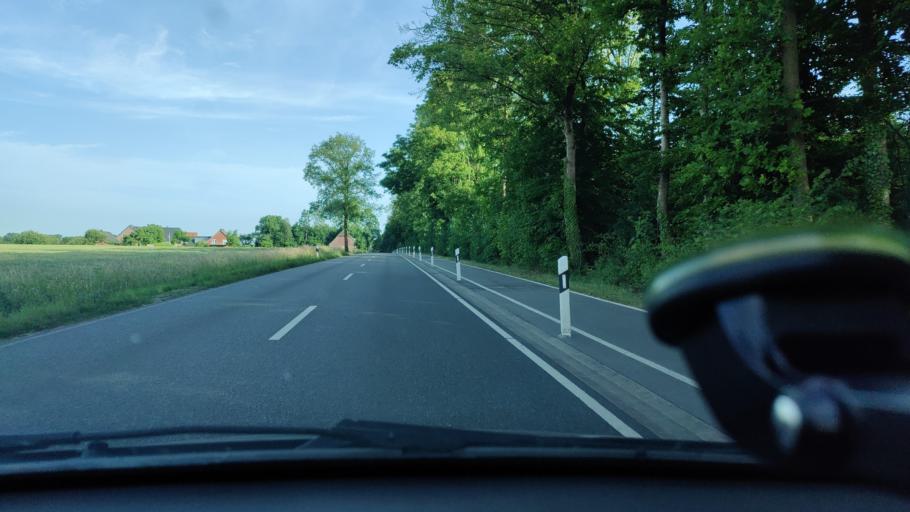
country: DE
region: North Rhine-Westphalia
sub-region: Regierungsbezirk Munster
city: Coesfeld
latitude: 51.9992
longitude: 7.1974
